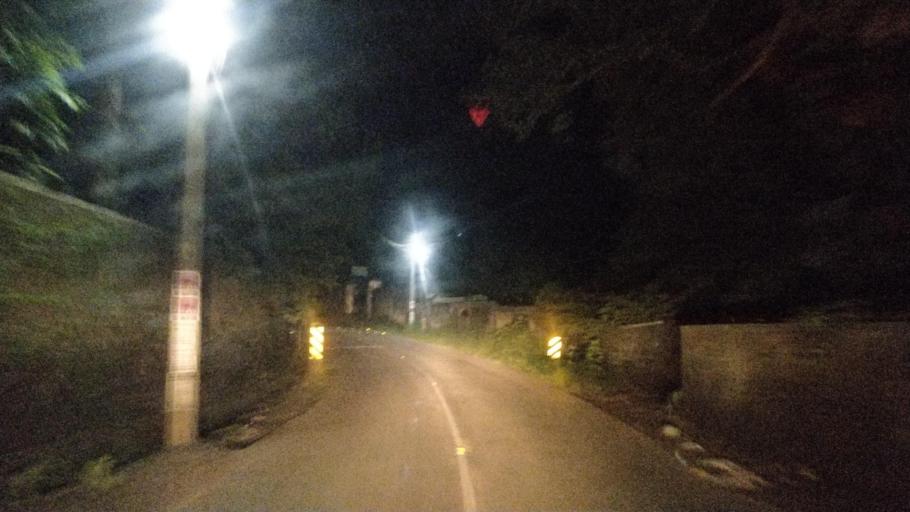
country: IN
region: Kerala
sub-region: Kottayam
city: Kottayam
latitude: 9.6411
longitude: 76.5095
